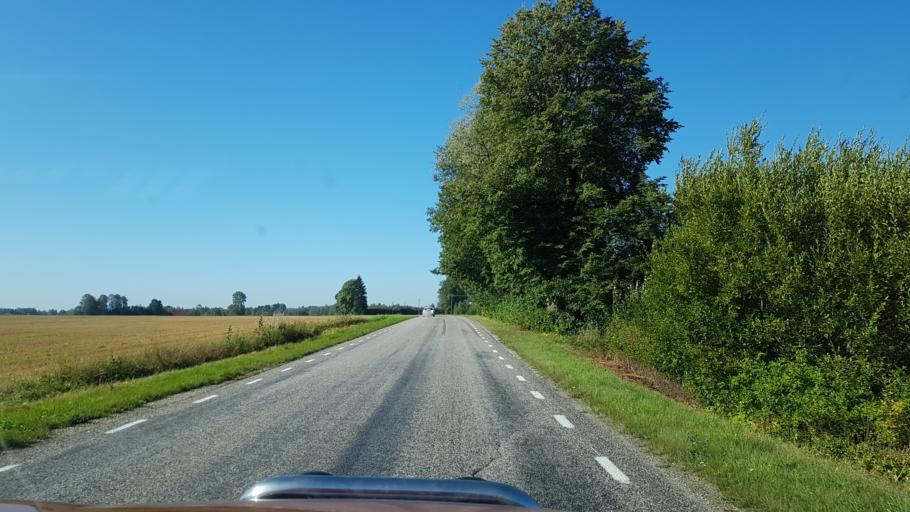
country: EE
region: Jogevamaa
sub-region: Jogeva linn
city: Jogeva
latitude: 58.6267
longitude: 26.3361
